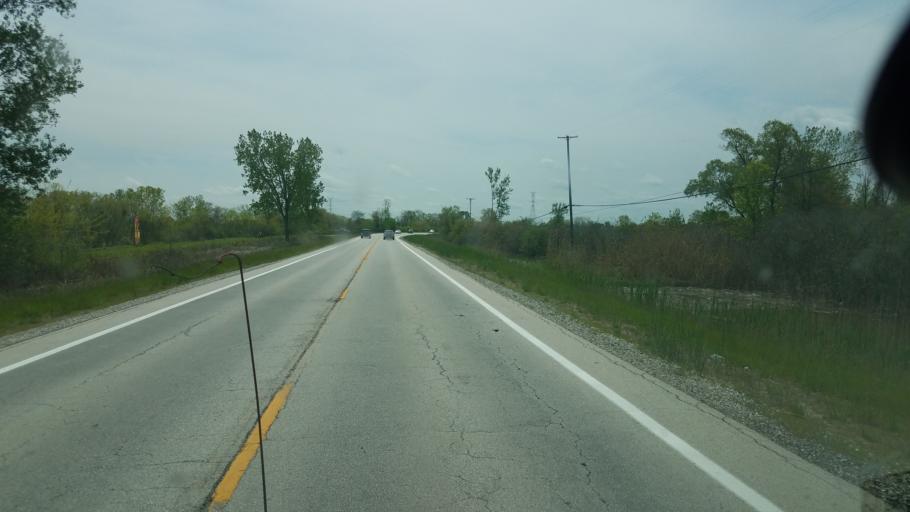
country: US
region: Ohio
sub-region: Ottawa County
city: Oak Harbor
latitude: 41.4508
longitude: -83.0554
